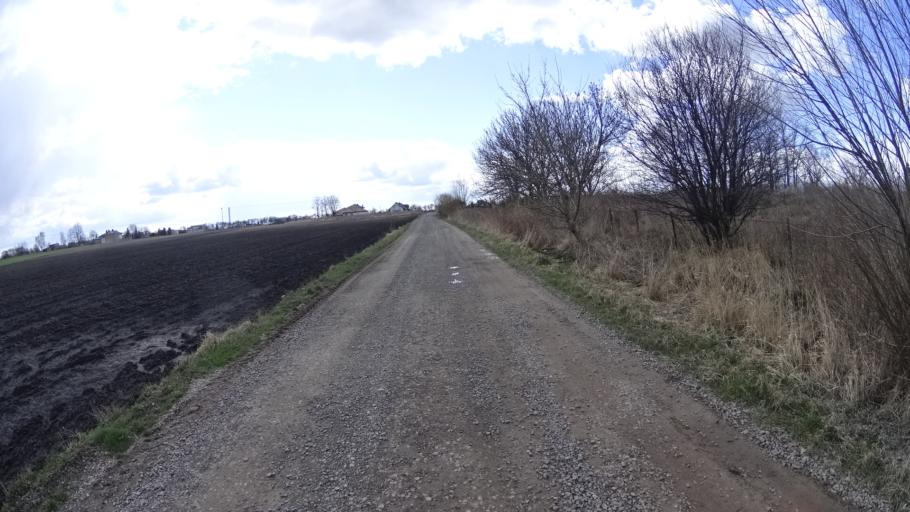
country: PL
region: Masovian Voivodeship
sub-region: Powiat warszawski zachodni
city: Jozefow
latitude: 52.2202
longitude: 20.7238
